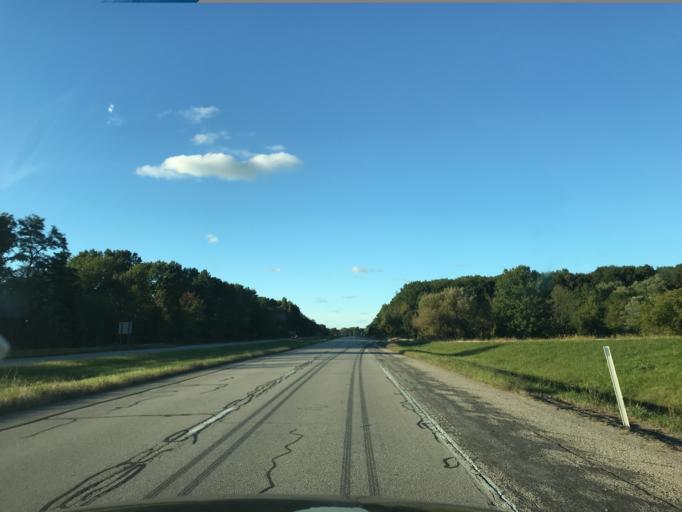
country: US
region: Ohio
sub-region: Ashtabula County
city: Edgewood
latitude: 41.8901
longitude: -80.7810
